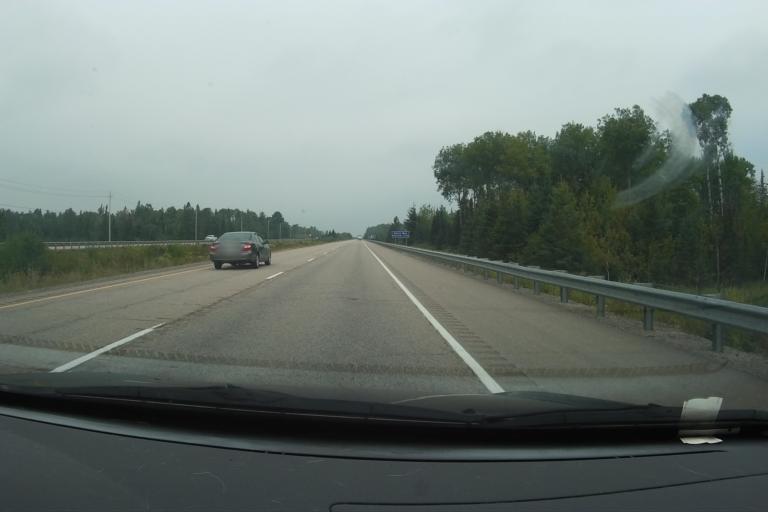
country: CA
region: Ontario
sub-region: Nipissing District
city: North Bay
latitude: 46.2432
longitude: -79.3594
